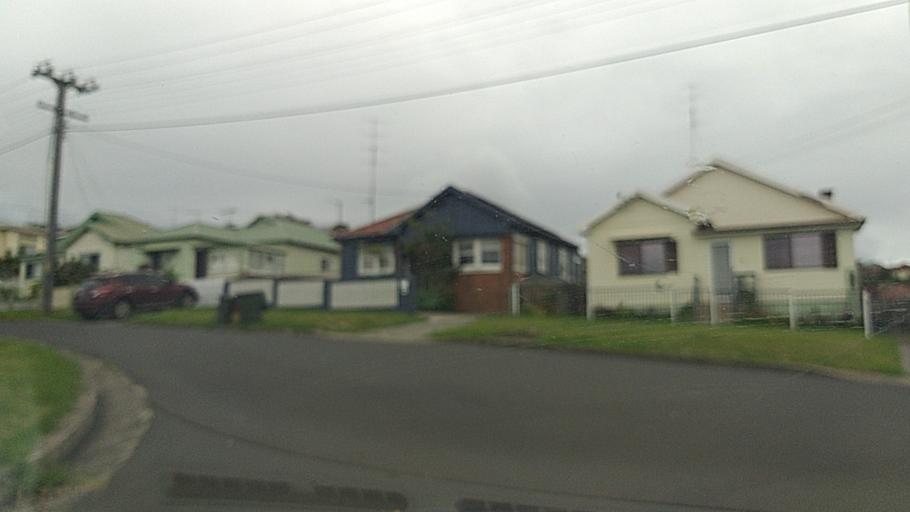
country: AU
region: New South Wales
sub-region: Wollongong
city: Lake Heights
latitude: -34.4849
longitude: 150.8843
